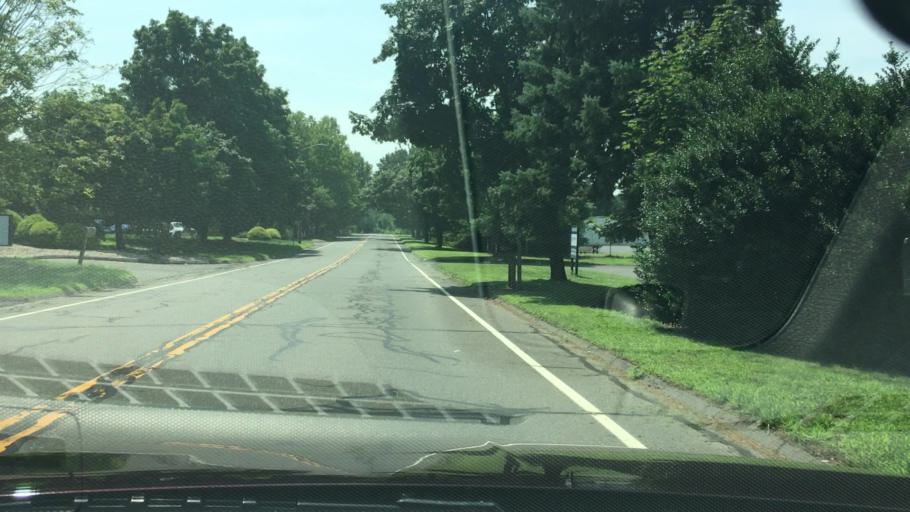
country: US
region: Connecticut
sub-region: Hartford County
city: South Windsor
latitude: 41.8302
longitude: -72.5995
